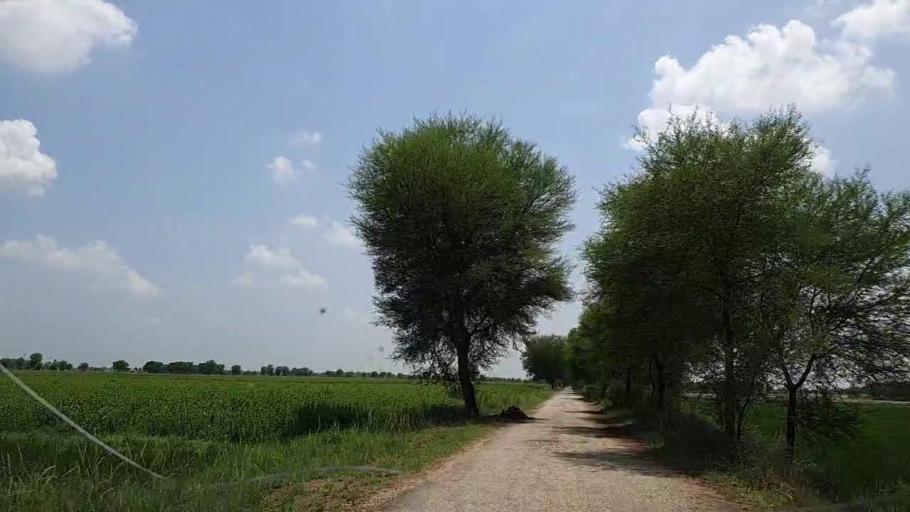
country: PK
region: Sindh
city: Tharu Shah
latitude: 27.0170
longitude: 68.0708
